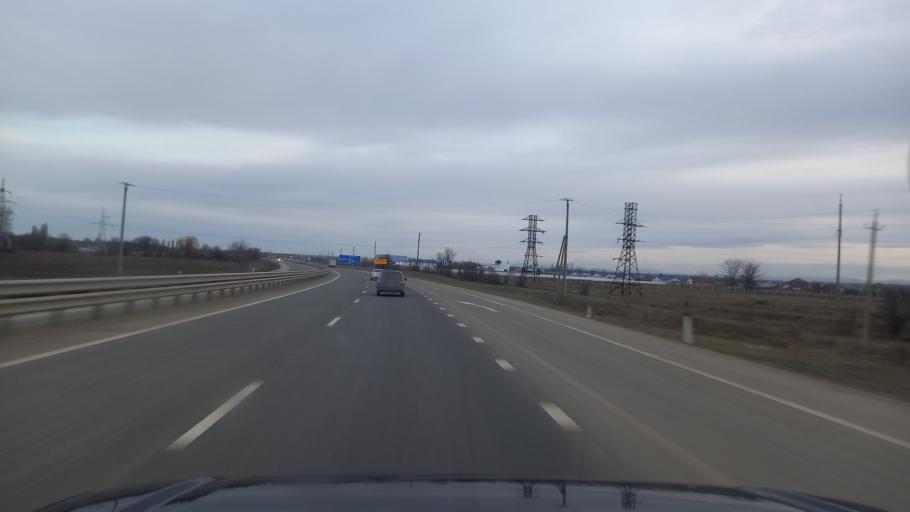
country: RU
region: Adygeya
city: Khanskaya
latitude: 44.6931
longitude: 39.9713
